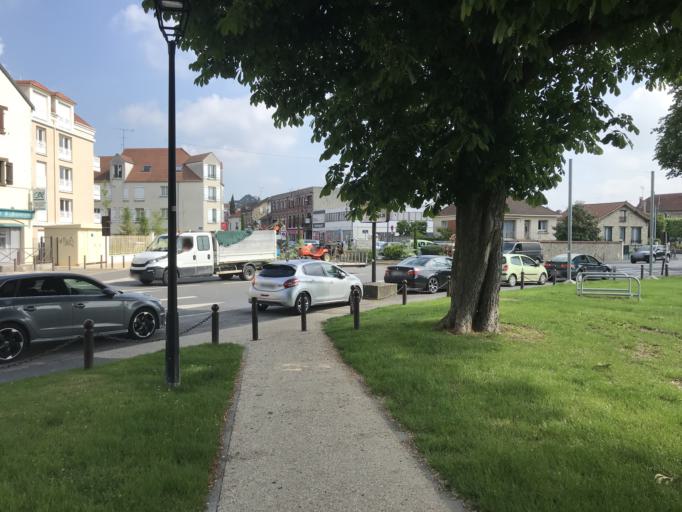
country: FR
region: Ile-de-France
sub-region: Departement de Seine-et-Marne
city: Esbly
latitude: 48.9003
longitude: 2.8118
